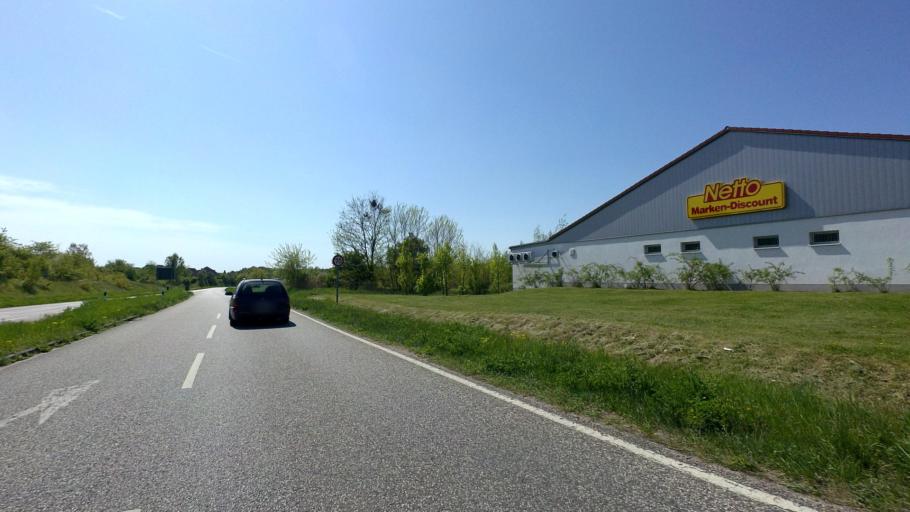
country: DE
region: Brandenburg
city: Konigs Wusterhausen
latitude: 52.3020
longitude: 13.6022
